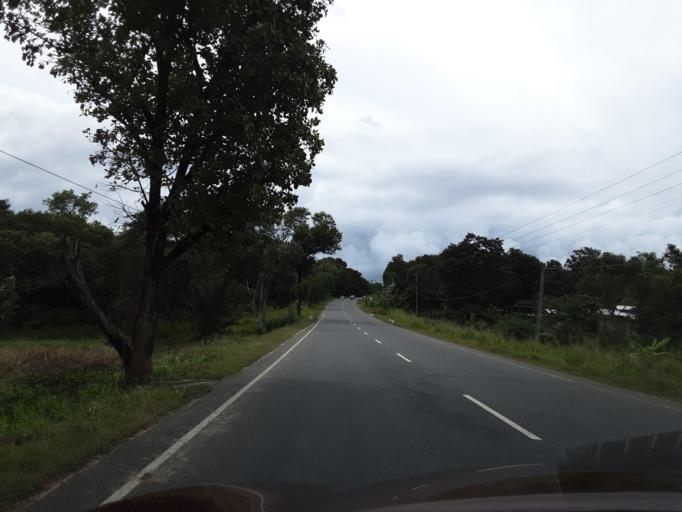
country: LK
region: Uva
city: Badulla
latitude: 7.3878
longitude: 81.1457
